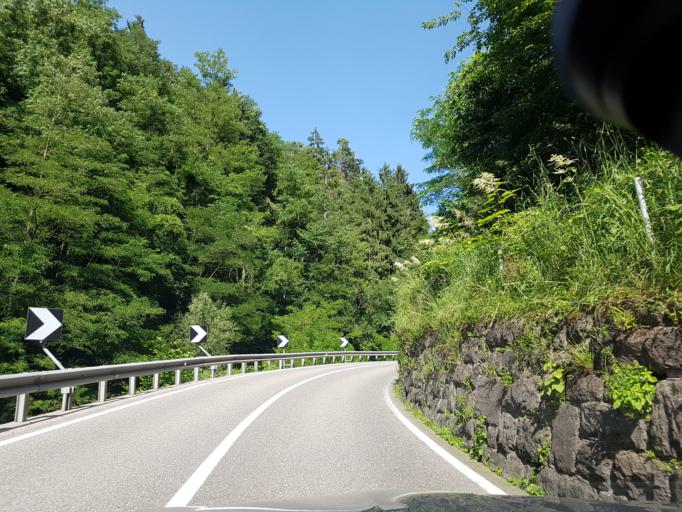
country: IT
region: Trentino-Alto Adige
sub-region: Bolzano
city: Ponte Gardena
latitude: 46.5989
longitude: 11.5388
